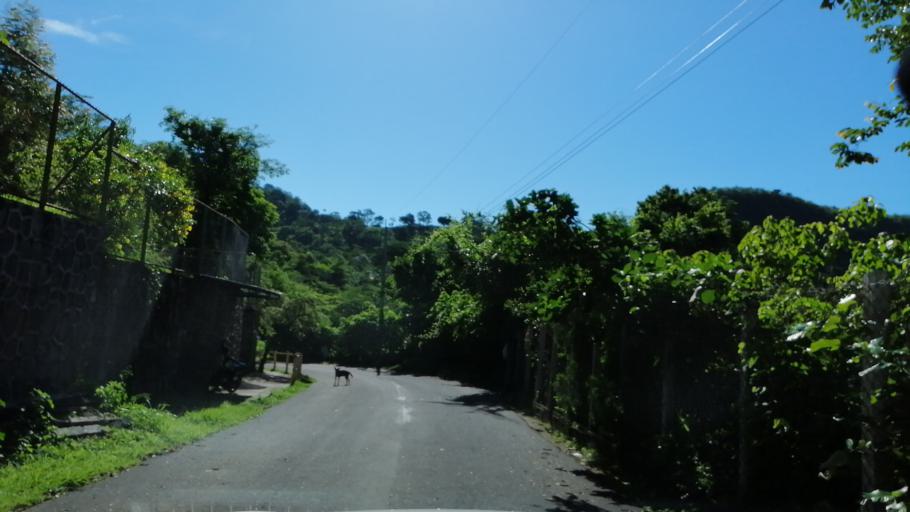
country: SV
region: Morazan
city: Corinto
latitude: 13.7947
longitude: -88.0118
